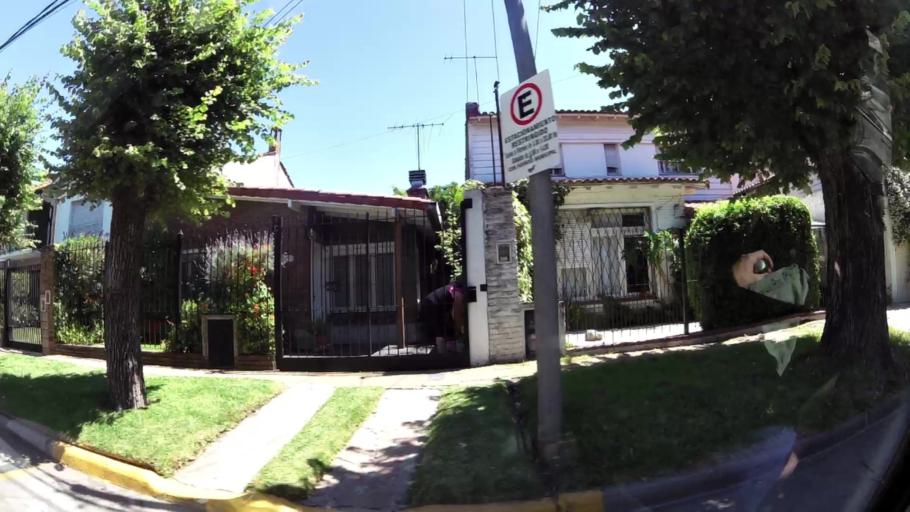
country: AR
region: Buenos Aires
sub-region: Partido de San Isidro
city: San Isidro
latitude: -34.4833
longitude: -58.5116
